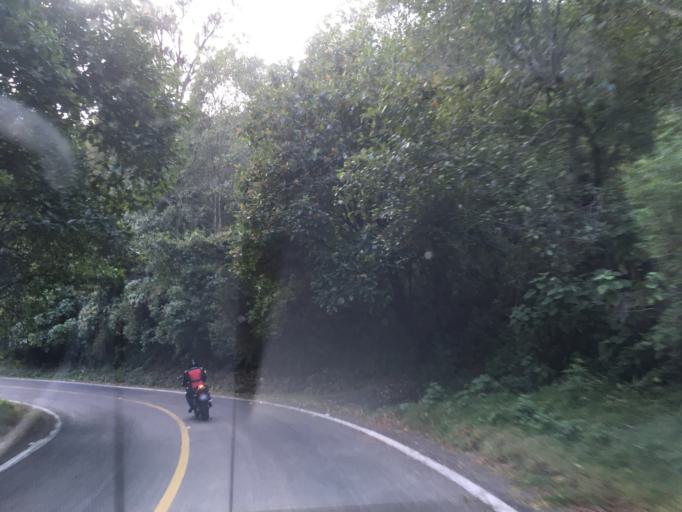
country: MX
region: Michoacan
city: Tzitzio
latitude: 19.6821
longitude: -100.8898
